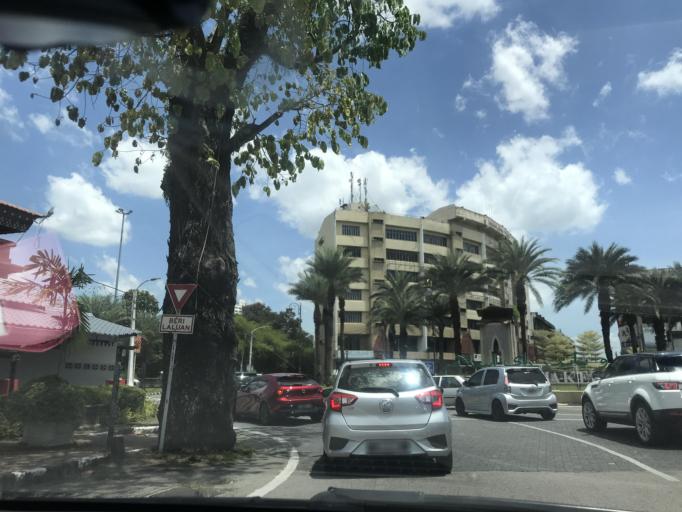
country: MY
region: Kelantan
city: Kota Bharu
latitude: 6.1252
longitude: 102.2381
